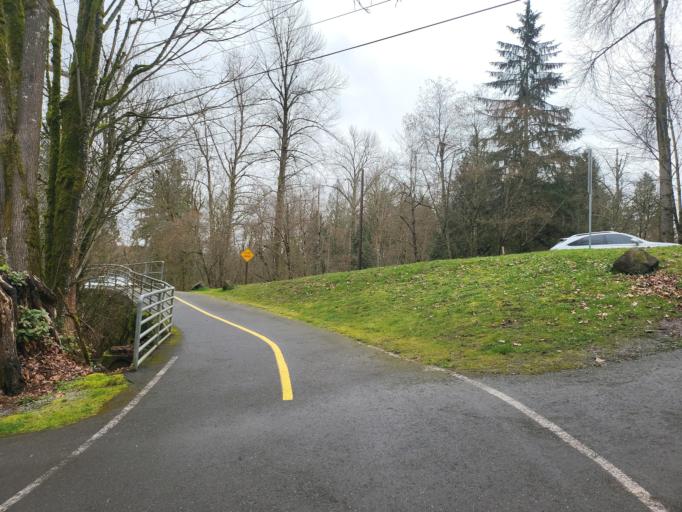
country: US
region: Washington
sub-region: King County
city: East Hill-Meridian
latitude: 47.4190
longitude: -122.1630
